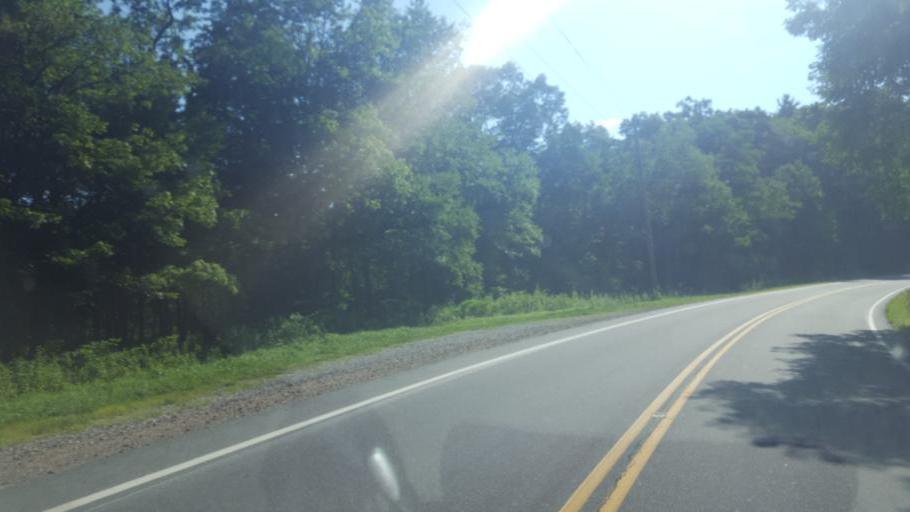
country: US
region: North Carolina
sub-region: Avery County
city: Newland
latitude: 36.0350
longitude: -81.9108
